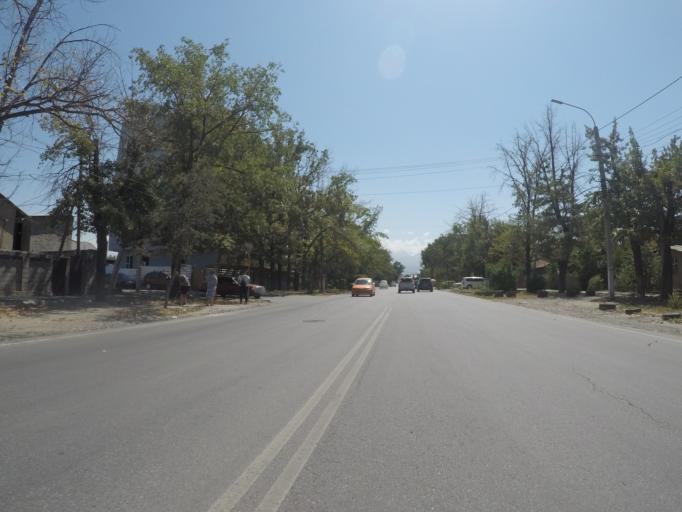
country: KG
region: Chuy
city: Bishkek
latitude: 42.8460
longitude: 74.5769
